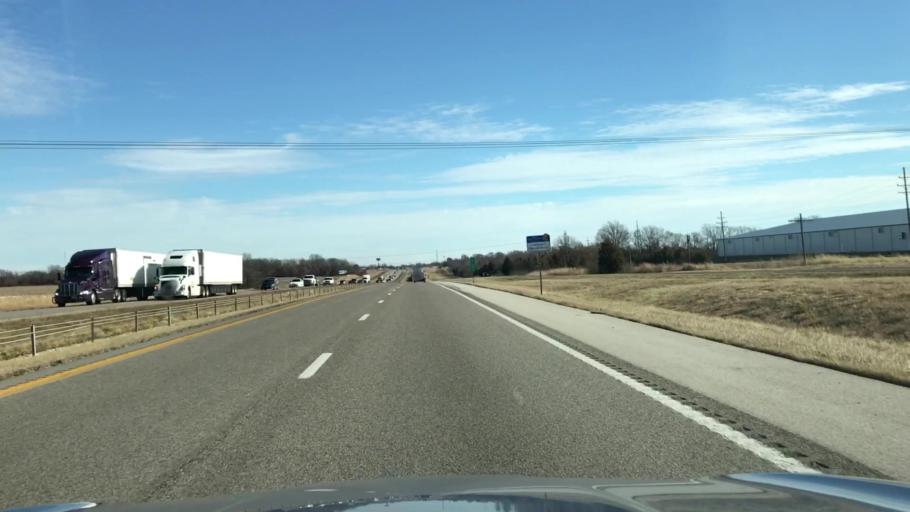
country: US
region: Missouri
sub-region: Warren County
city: Wright City
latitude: 38.8251
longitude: -90.9985
